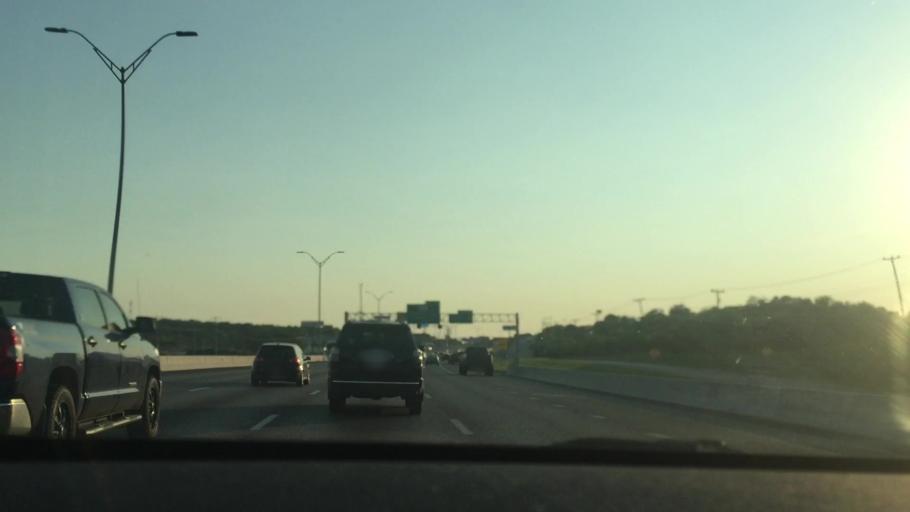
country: US
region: Texas
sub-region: Bexar County
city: Live Oak
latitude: 29.5555
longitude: -98.3481
